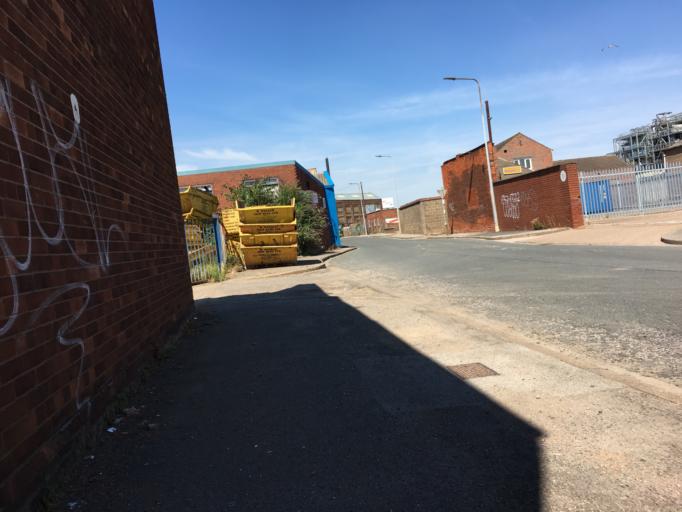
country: GB
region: England
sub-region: City of Kingston upon Hull
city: Hull
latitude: 53.7545
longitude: -0.3306
